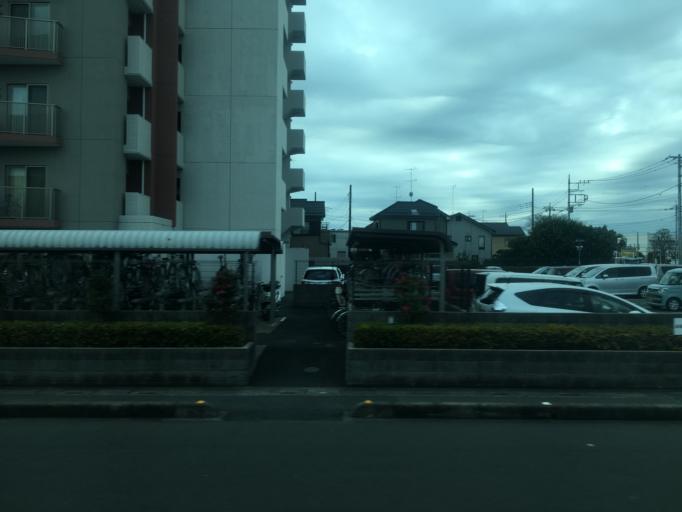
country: JP
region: Saitama
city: Okegawa
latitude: 35.9869
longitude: 139.5759
